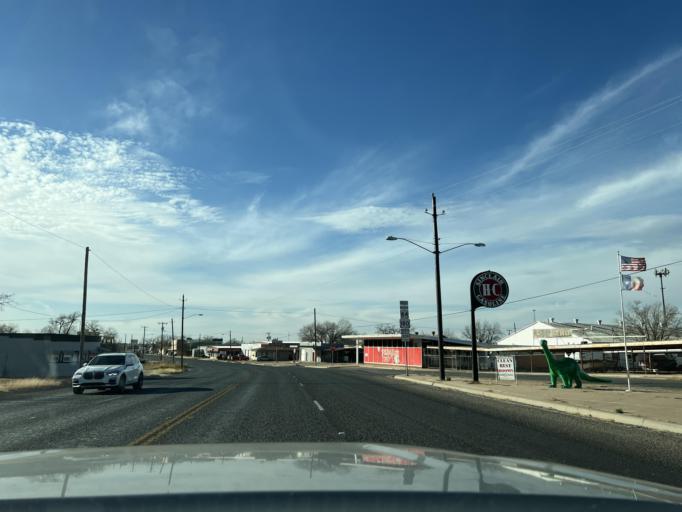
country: US
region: Texas
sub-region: Scurry County
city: Snyder
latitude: 32.7167
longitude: -100.9044
